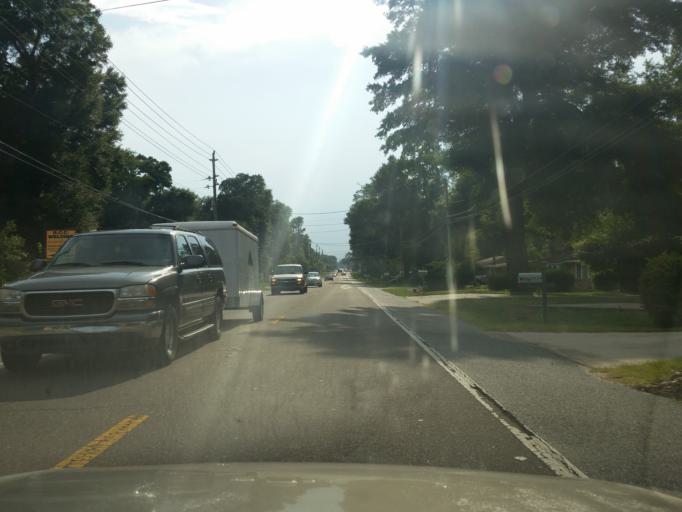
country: US
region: Florida
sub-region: Escambia County
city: Ferry Pass
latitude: 30.5100
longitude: -87.2019
